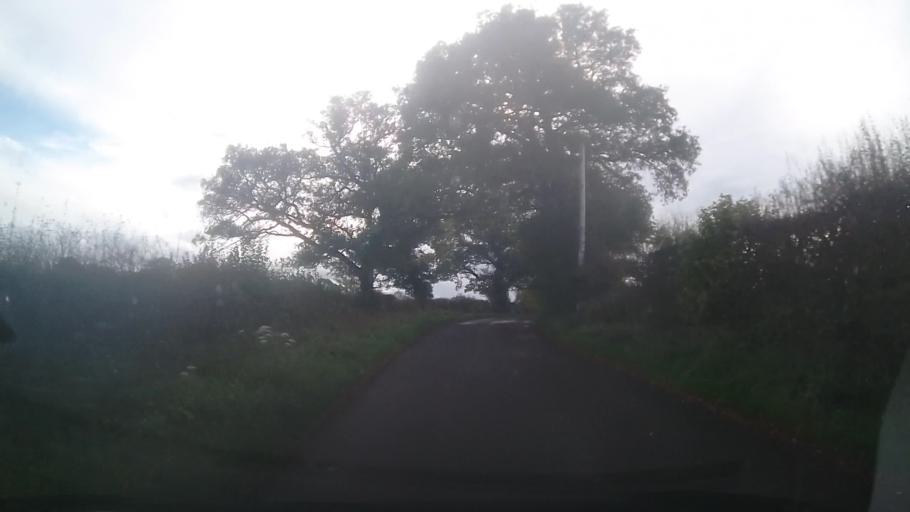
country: GB
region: England
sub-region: Shropshire
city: Whitchurch
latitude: 52.9373
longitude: -2.7208
